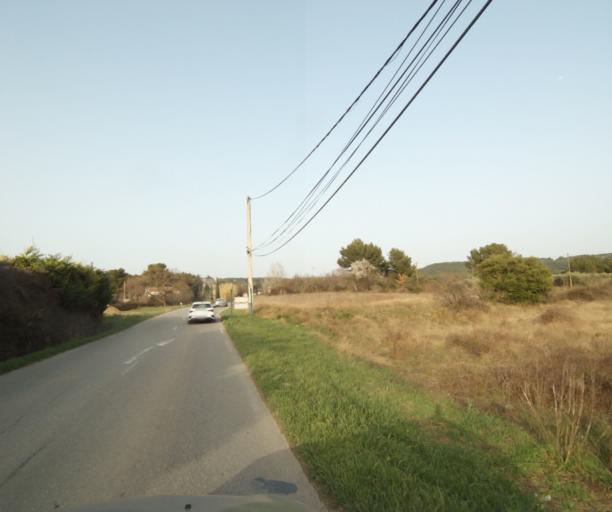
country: FR
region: Provence-Alpes-Cote d'Azur
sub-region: Departement des Bouches-du-Rhone
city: Eguilles
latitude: 43.5594
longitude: 5.3516
